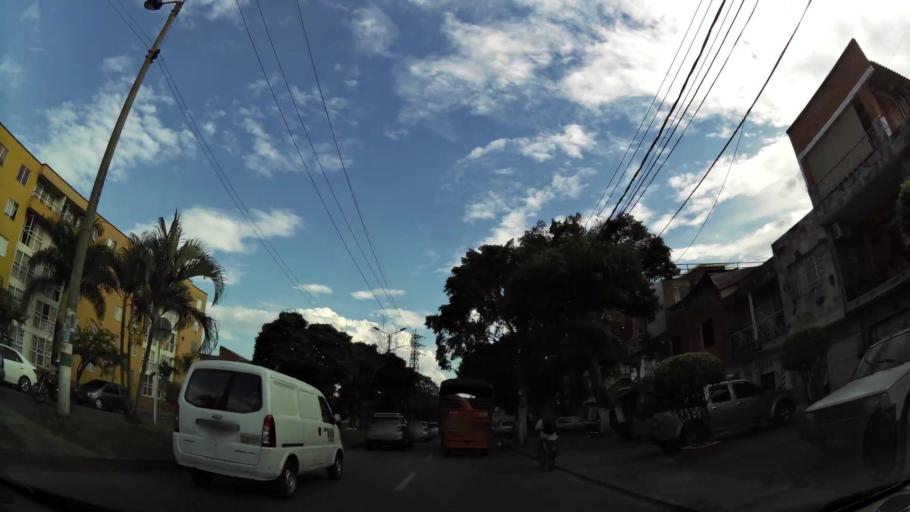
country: CO
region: Valle del Cauca
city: Cali
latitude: 3.4624
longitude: -76.5076
